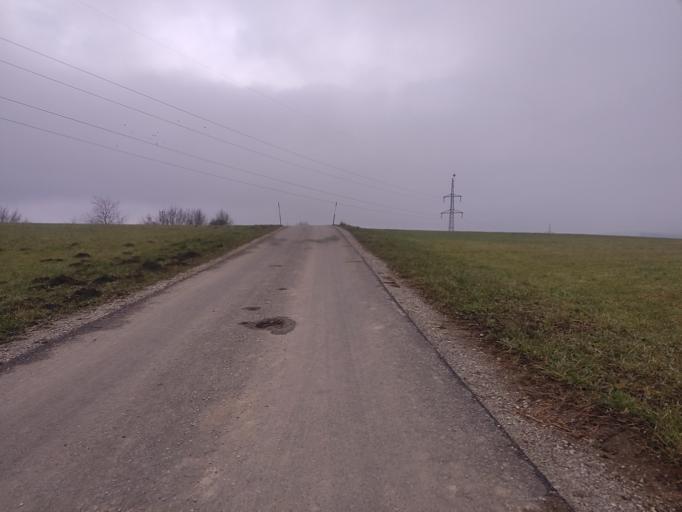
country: AT
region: Salzburg
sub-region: Politischer Bezirk Salzburg-Umgebung
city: Kostendorf
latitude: 47.9538
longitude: 13.1974
